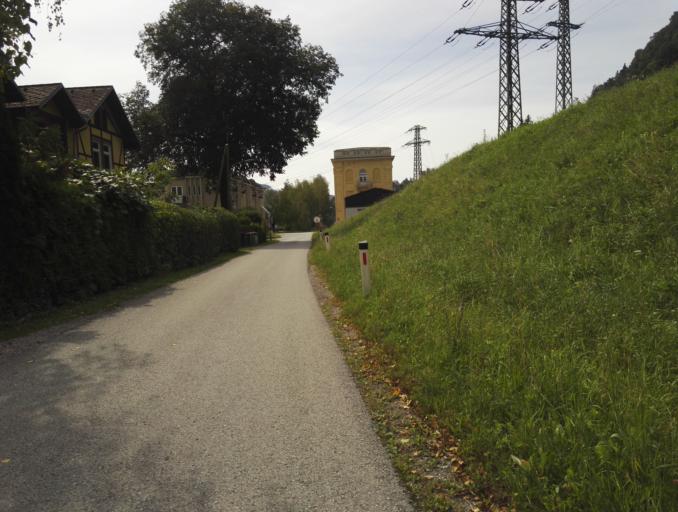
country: AT
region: Styria
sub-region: Politischer Bezirk Graz-Umgebung
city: Peggau
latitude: 47.2106
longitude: 15.3358
